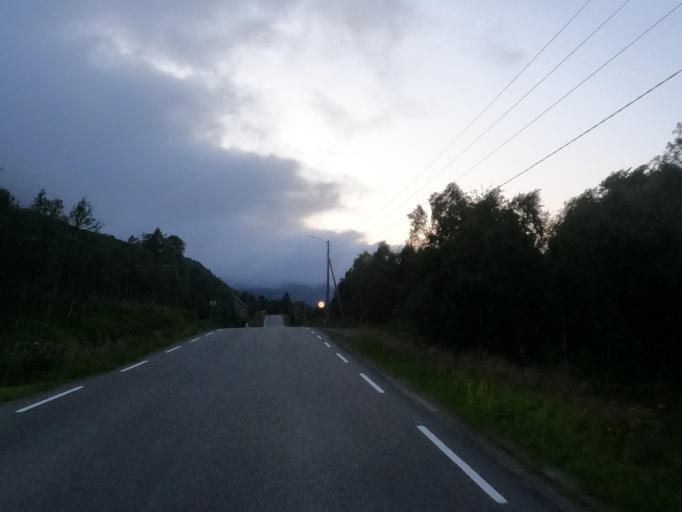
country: NO
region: Nordland
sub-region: Lodingen
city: Lodingen
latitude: 68.5816
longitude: 15.7924
